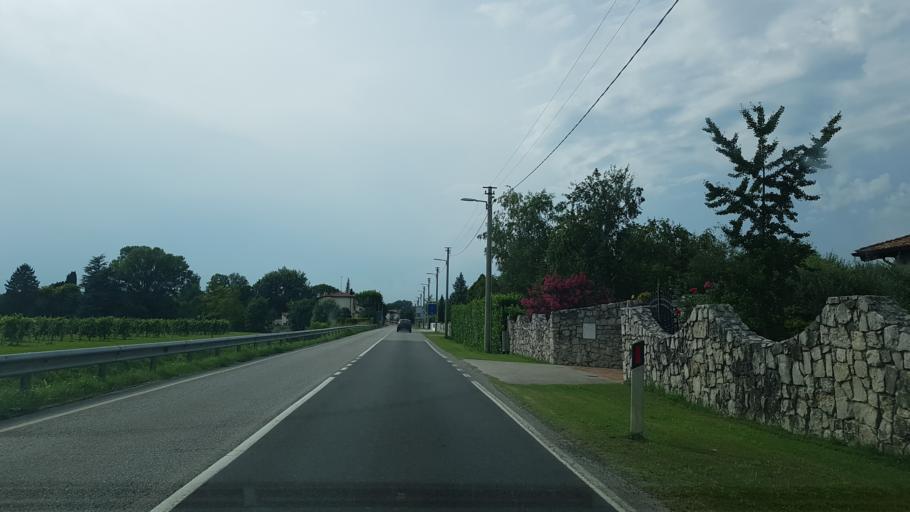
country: IT
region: Friuli Venezia Giulia
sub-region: Provincia di Gorizia
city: Pieris
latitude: 45.8025
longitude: 13.4505
